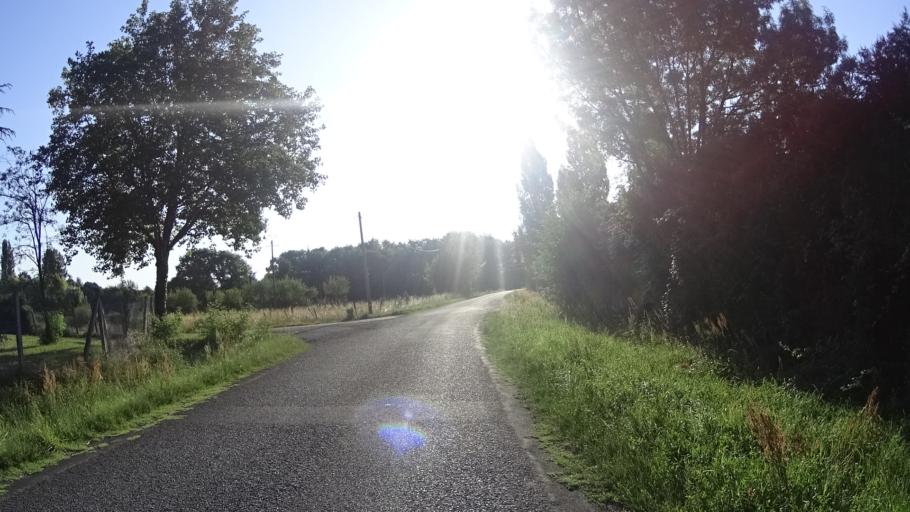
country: FR
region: Pays de la Loire
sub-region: Departement de Maine-et-Loire
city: Allonnes
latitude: 47.2704
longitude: 0.0029
